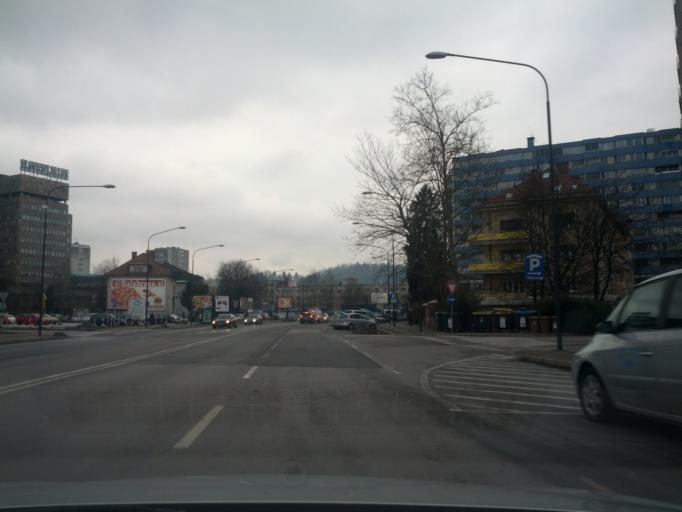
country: SI
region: Ljubljana
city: Ljubljana
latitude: 46.0637
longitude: 14.5118
